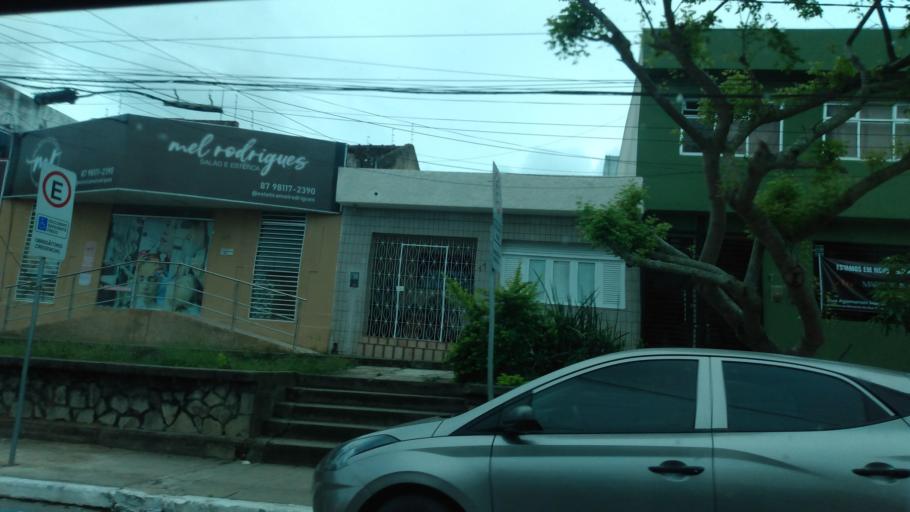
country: BR
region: Pernambuco
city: Garanhuns
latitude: -8.8894
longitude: -36.4948
